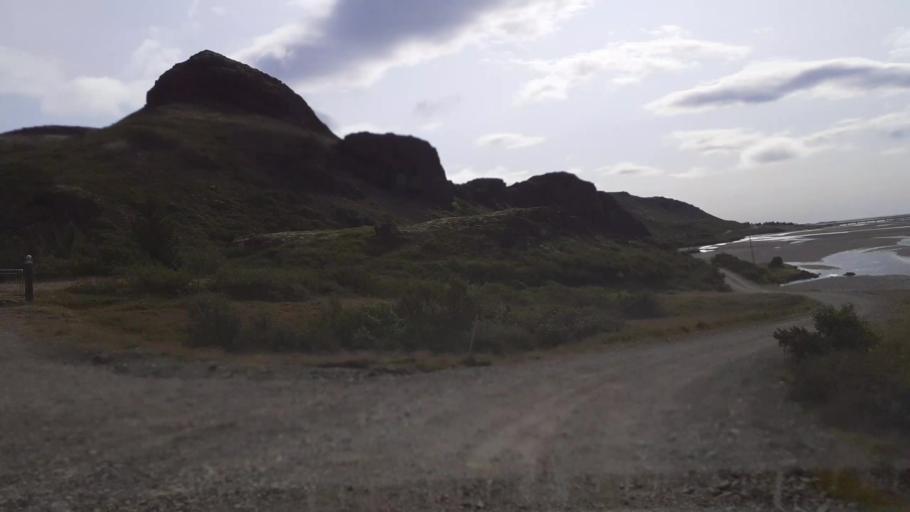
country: IS
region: East
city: Hoefn
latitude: 64.4350
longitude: -14.8969
